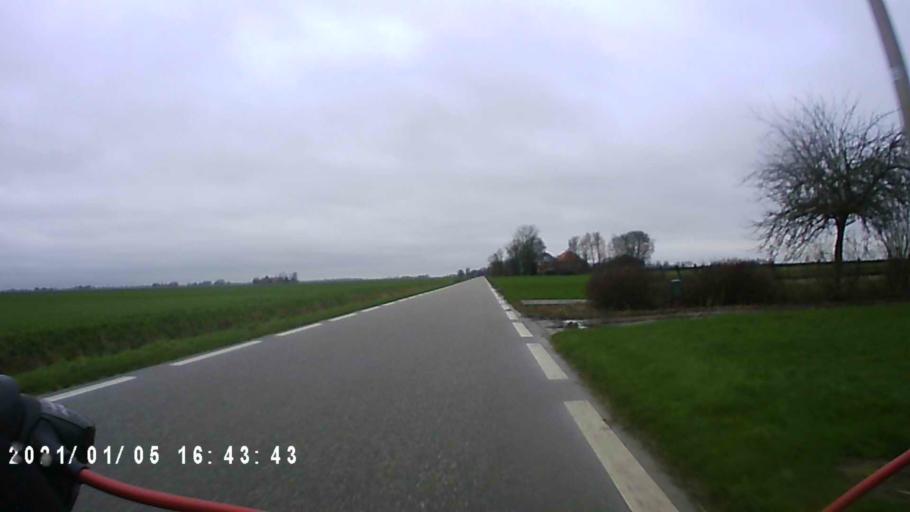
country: NL
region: Groningen
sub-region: Gemeente  Oldambt
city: Winschoten
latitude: 53.2156
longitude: 7.0514
